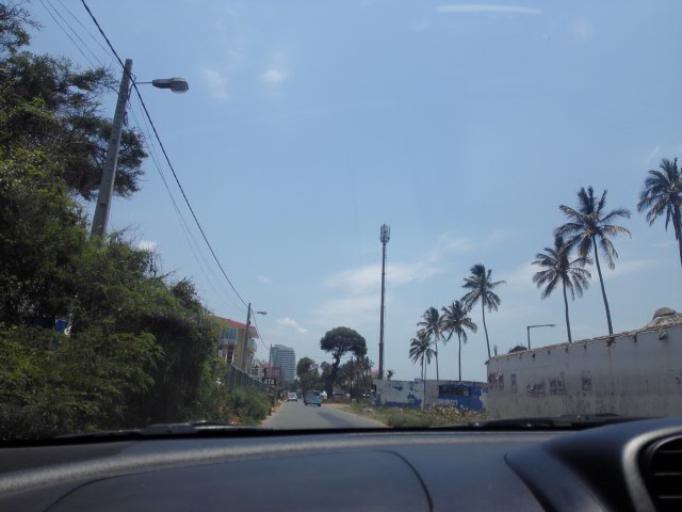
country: MZ
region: Maputo City
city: Maputo
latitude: -25.9643
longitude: 32.6024
